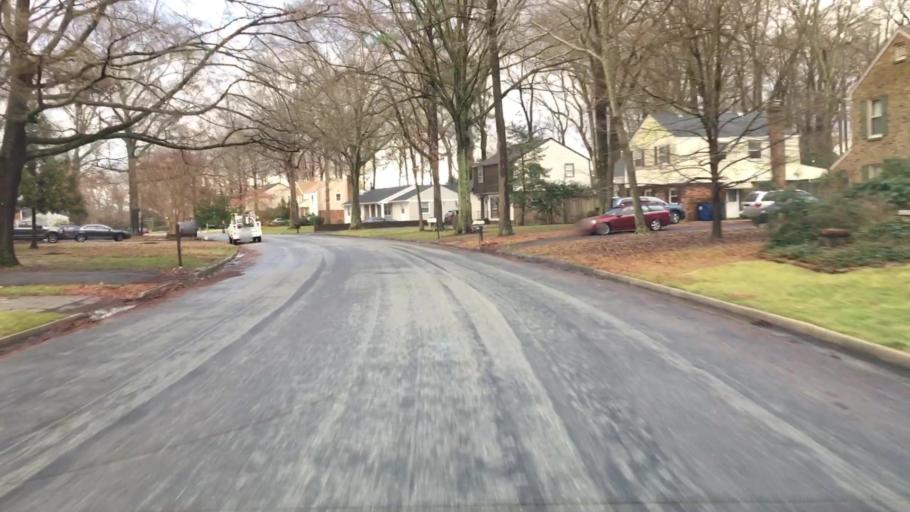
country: US
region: Virginia
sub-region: Chesterfield County
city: Bon Air
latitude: 37.5122
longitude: -77.6191
